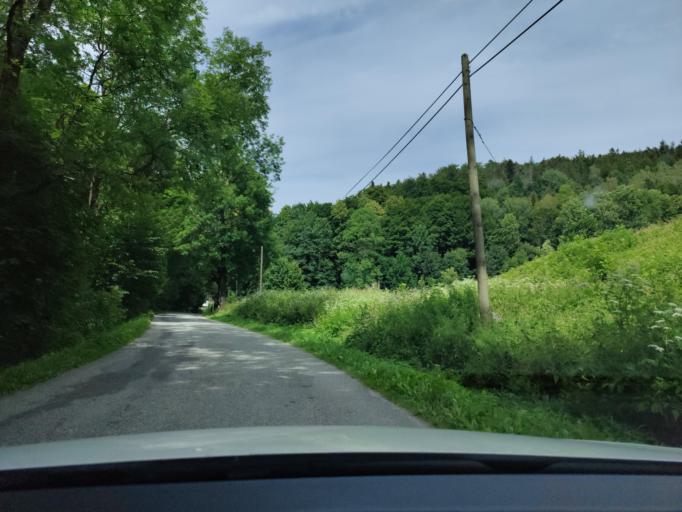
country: CZ
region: Olomoucky
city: Zlate Hory
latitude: 50.2323
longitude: 17.3447
